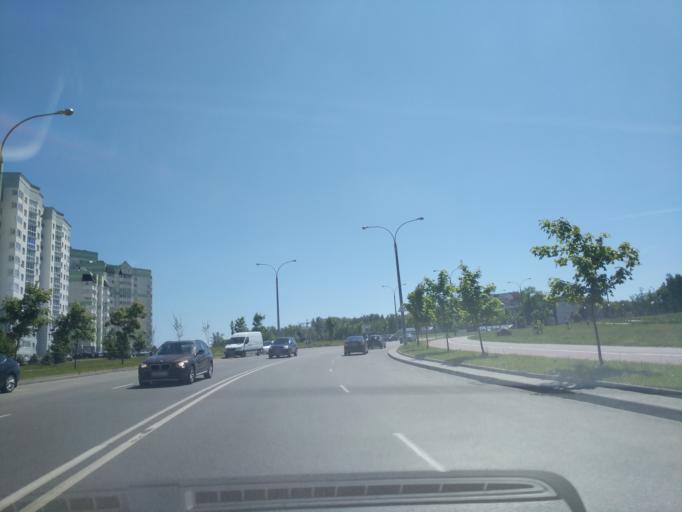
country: BY
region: Minsk
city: Zhdanovichy
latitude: 53.9110
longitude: 27.4175
